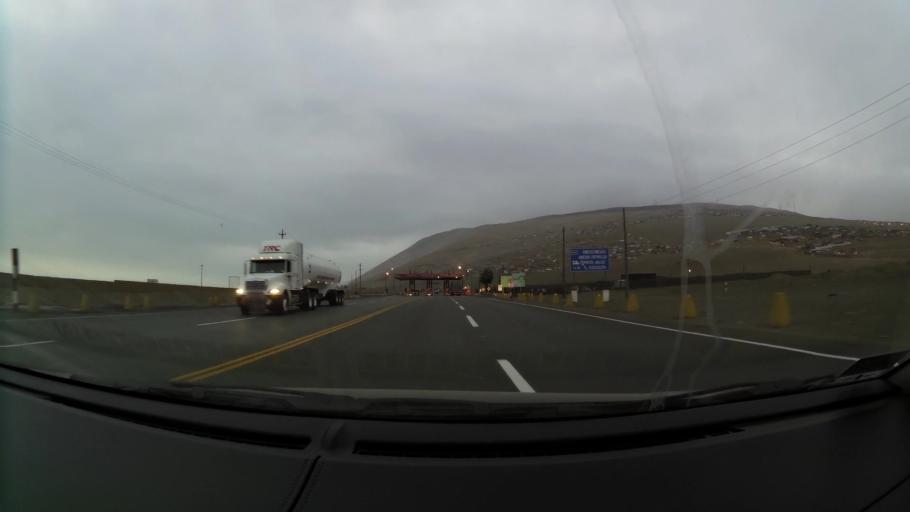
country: PE
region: Lima
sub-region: Lima
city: Santa Rosa
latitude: -11.7450
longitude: -77.1646
